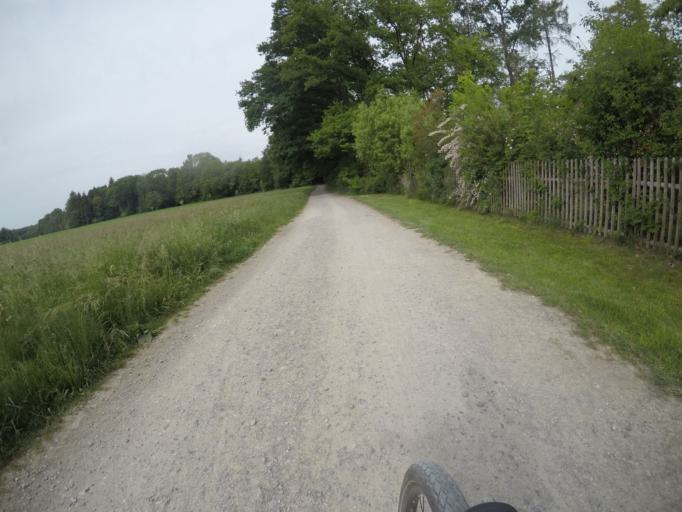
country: DE
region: Baden-Wuerttemberg
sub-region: Regierungsbezirk Stuttgart
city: Waldenbuch
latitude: 48.5927
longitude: 9.1464
